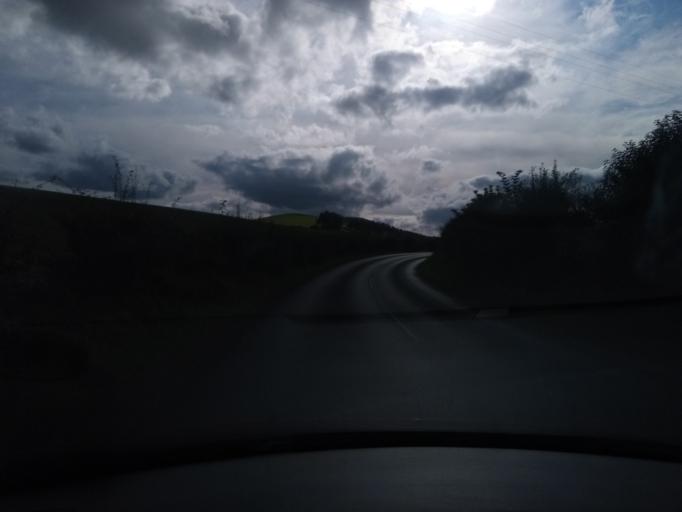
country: GB
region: Scotland
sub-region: The Scottish Borders
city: Kelso
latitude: 55.5201
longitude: -2.3545
